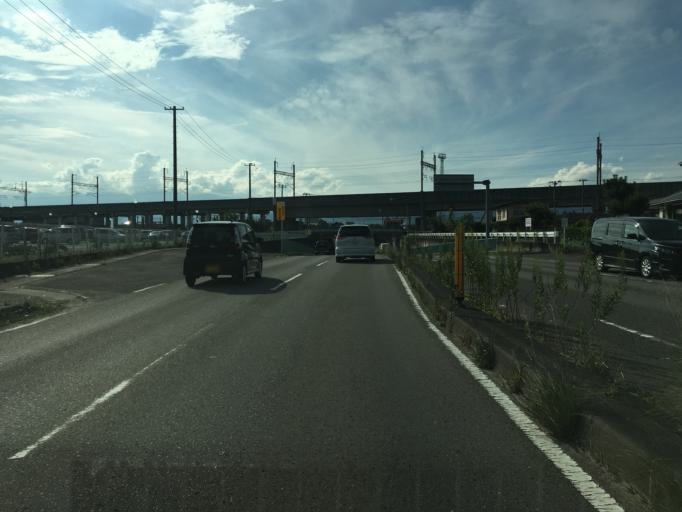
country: JP
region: Fukushima
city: Fukushima-shi
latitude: 37.7974
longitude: 140.4785
